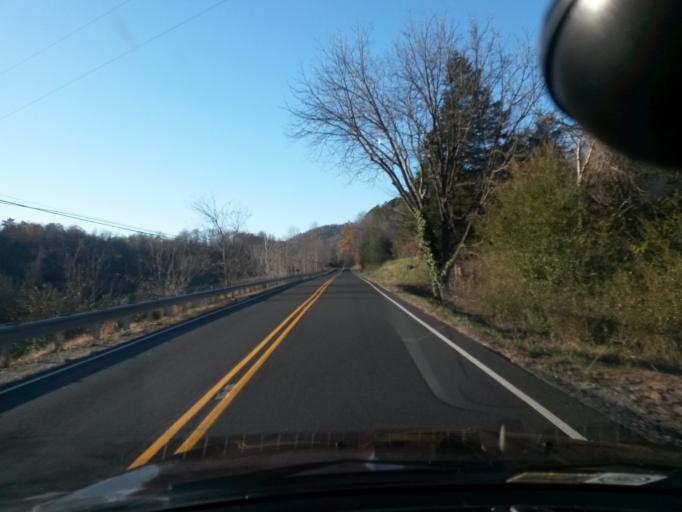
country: US
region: Virginia
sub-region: Amherst County
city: Amherst
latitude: 37.6613
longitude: -79.1569
